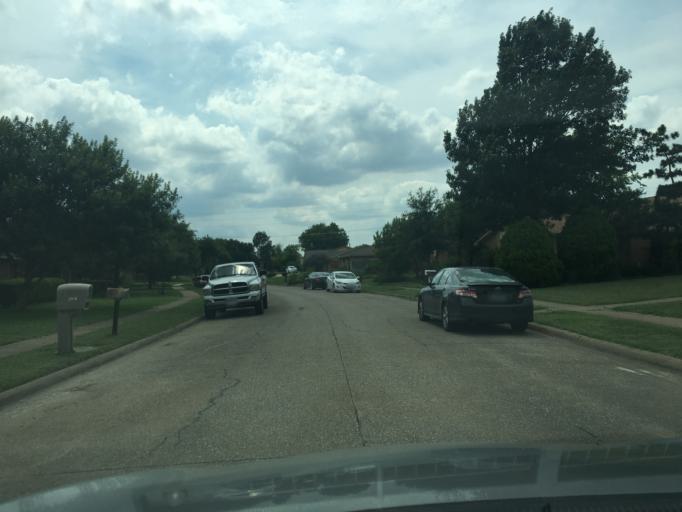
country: US
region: Texas
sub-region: Dallas County
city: Garland
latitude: 32.9553
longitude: -96.6723
